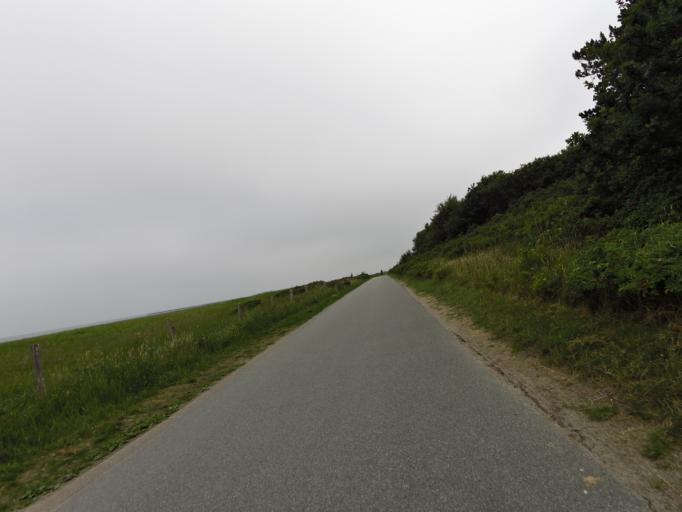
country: DE
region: Lower Saxony
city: Nordholz
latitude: 53.8674
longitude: 8.6009
